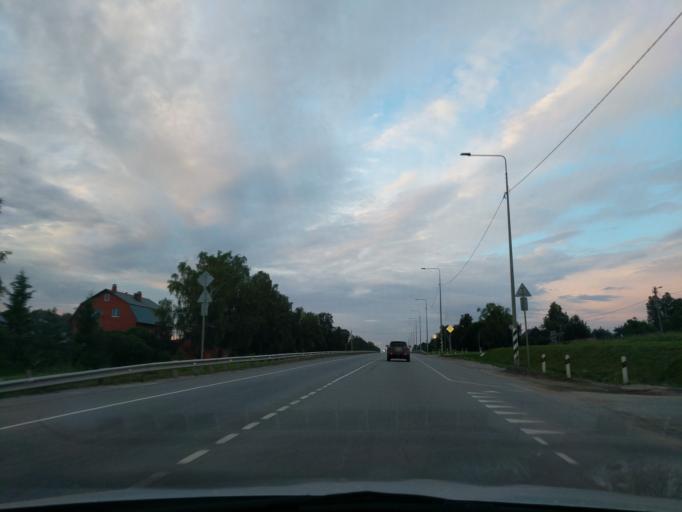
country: RU
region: Kaluga
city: Maloyaroslavets
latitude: 55.0293
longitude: 36.5220
